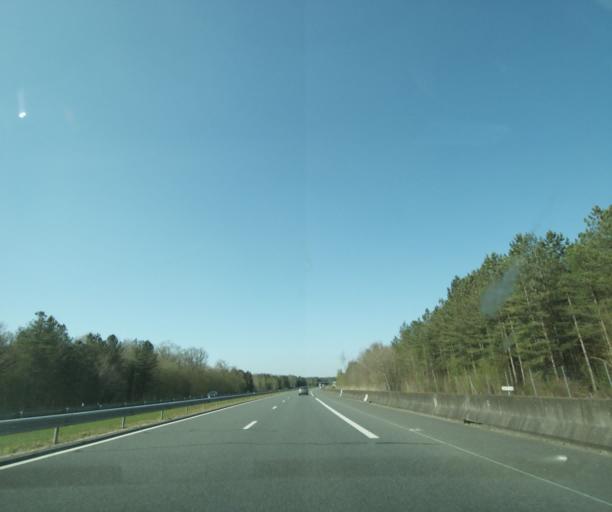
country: FR
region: Centre
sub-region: Departement du Loiret
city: Nogent-sur-Vernisson
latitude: 47.7733
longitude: 2.7115
